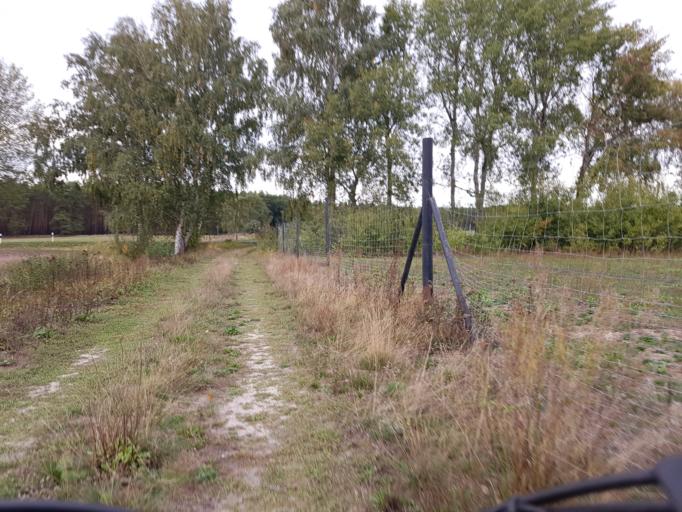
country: DE
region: Brandenburg
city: Schilda
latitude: 51.6103
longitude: 13.3806
